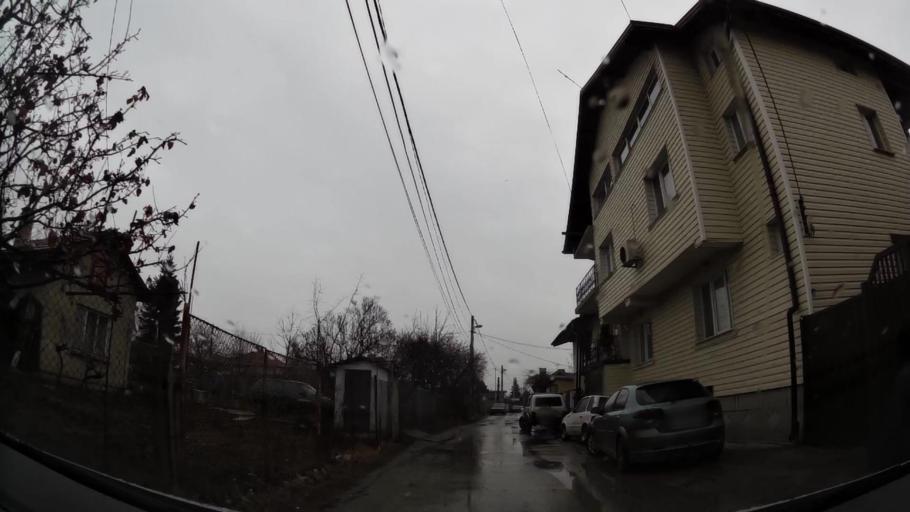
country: BG
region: Sofia-Capital
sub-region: Stolichna Obshtina
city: Sofia
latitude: 42.6546
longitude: 23.4285
